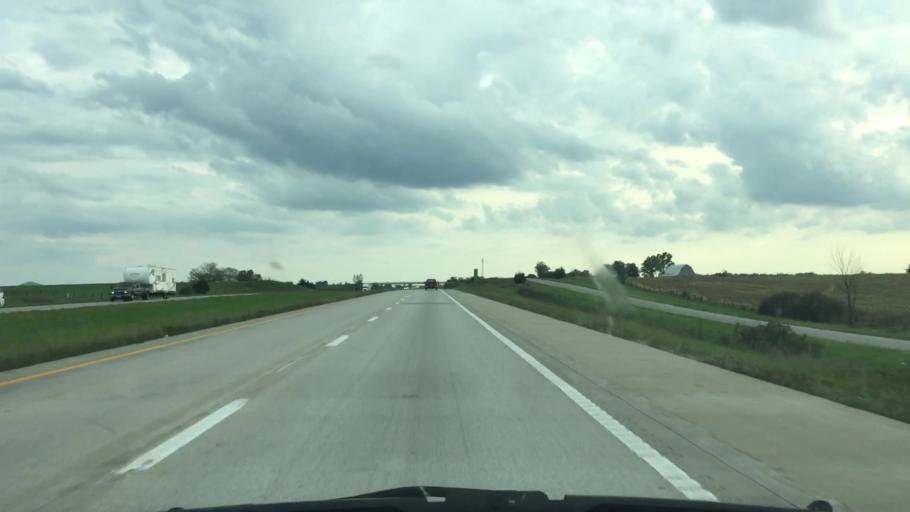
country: US
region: Missouri
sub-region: Clinton County
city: Lathrop
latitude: 39.5918
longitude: -94.2562
